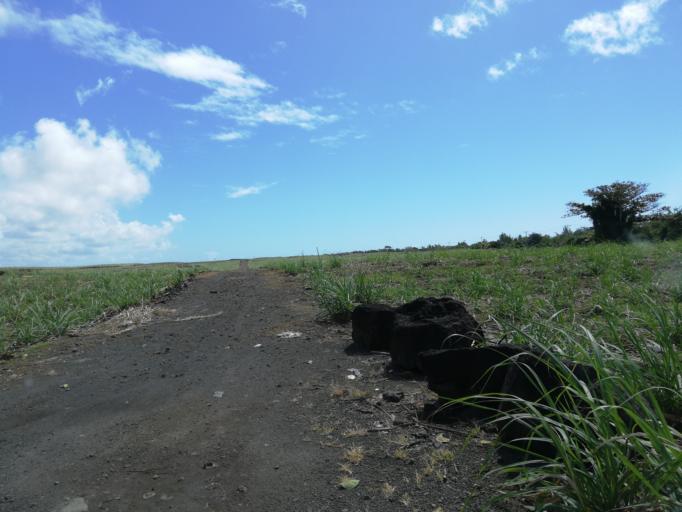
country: MU
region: Flacq
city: Bel Air Riviere Seche
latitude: -20.2557
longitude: 57.7792
